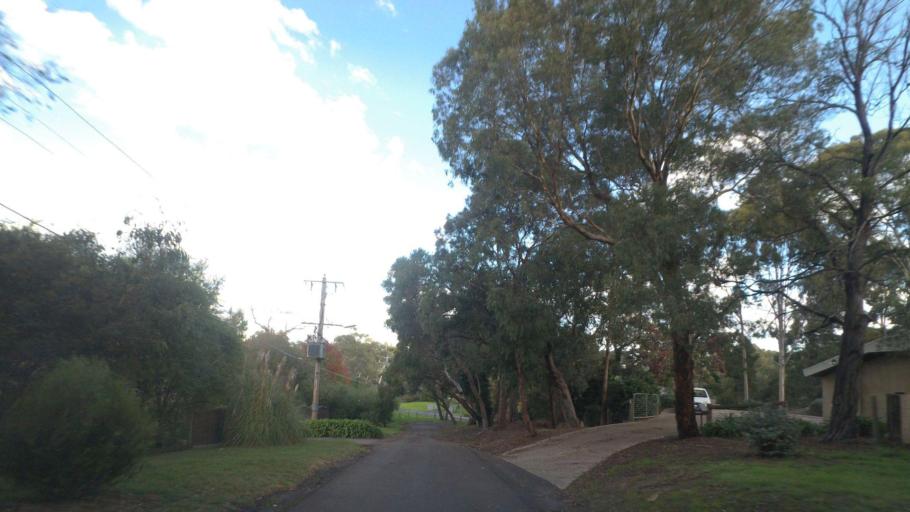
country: AU
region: Victoria
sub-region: Banyule
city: Lower Plenty
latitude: -37.7364
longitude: 145.1275
